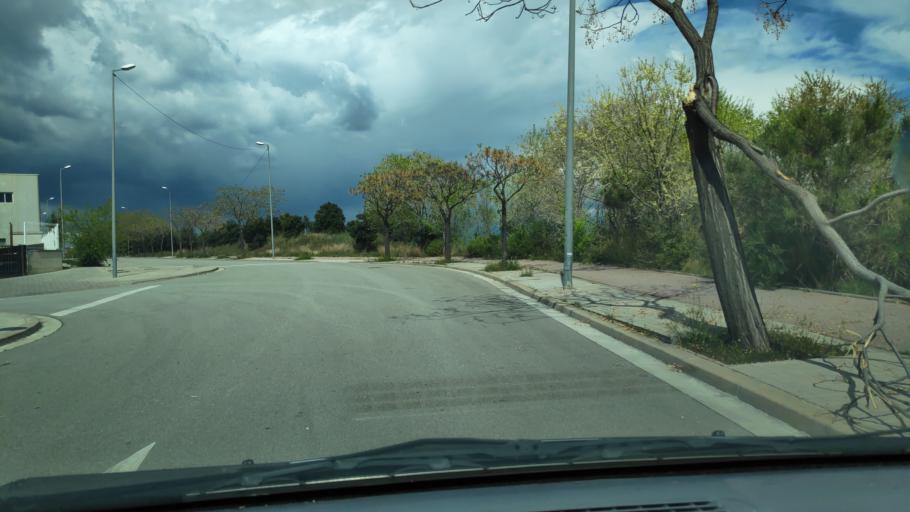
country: ES
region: Catalonia
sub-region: Provincia de Barcelona
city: Polinya
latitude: 41.5389
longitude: 2.1395
